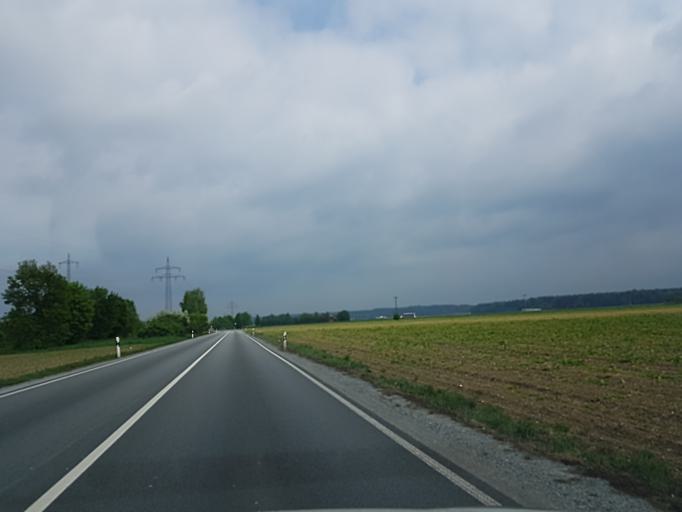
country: DE
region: Bavaria
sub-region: Upper Bavaria
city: Hohenlinden
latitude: 48.1505
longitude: 11.9941
